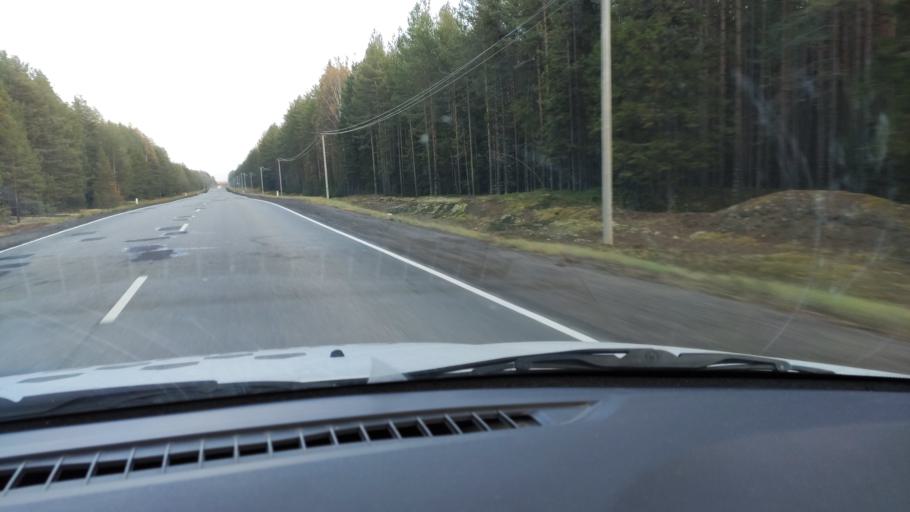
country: RU
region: Kirov
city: Belaya Kholunitsa
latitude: 58.9078
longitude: 50.9997
